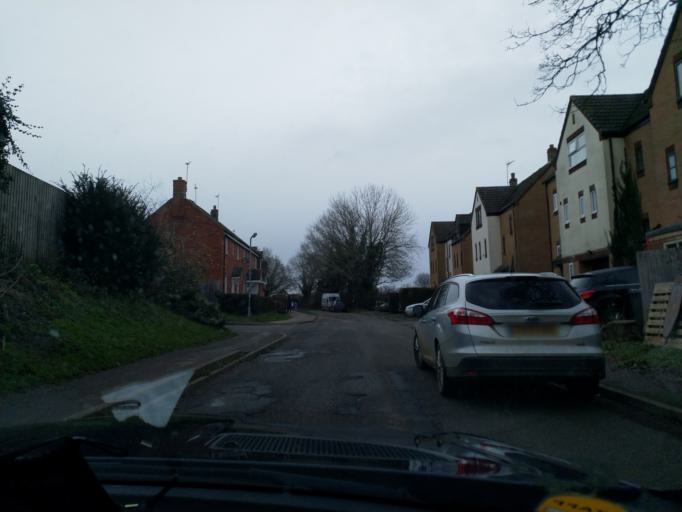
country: GB
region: England
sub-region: Oxfordshire
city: Adderbury
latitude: 52.0724
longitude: -1.2637
